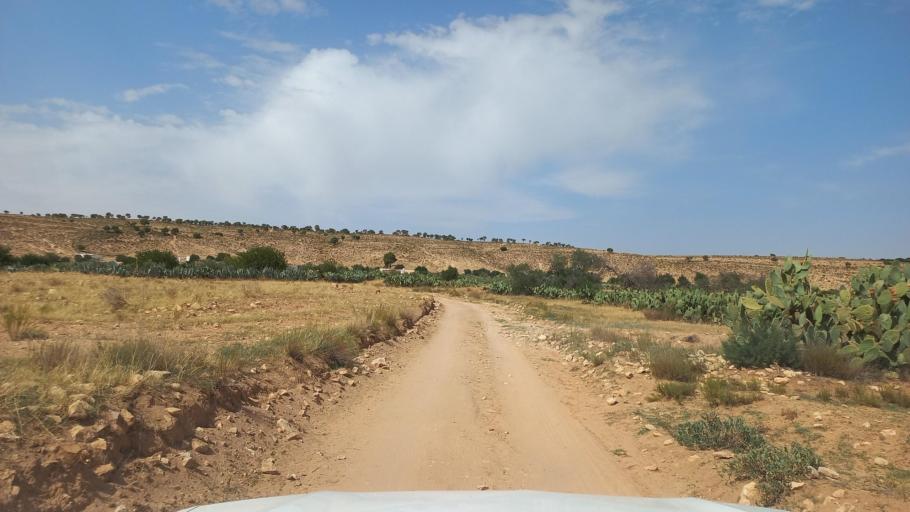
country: TN
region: Al Qasrayn
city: Kasserine
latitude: 35.3685
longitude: 8.8805
